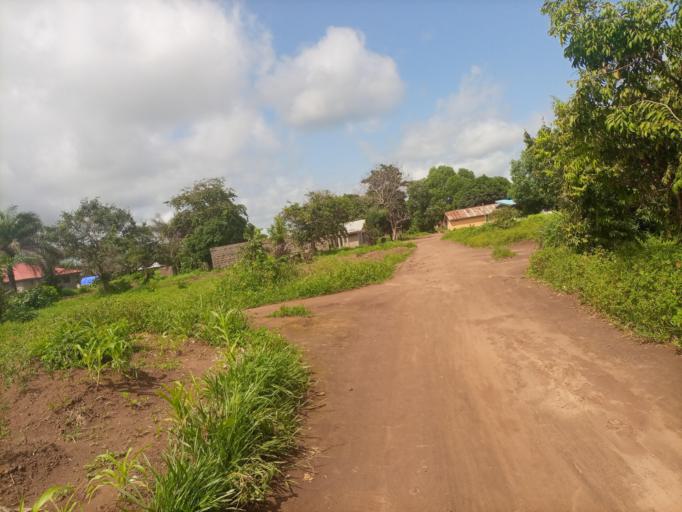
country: SL
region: Northern Province
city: Tintafor
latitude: 8.6383
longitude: -13.2129
